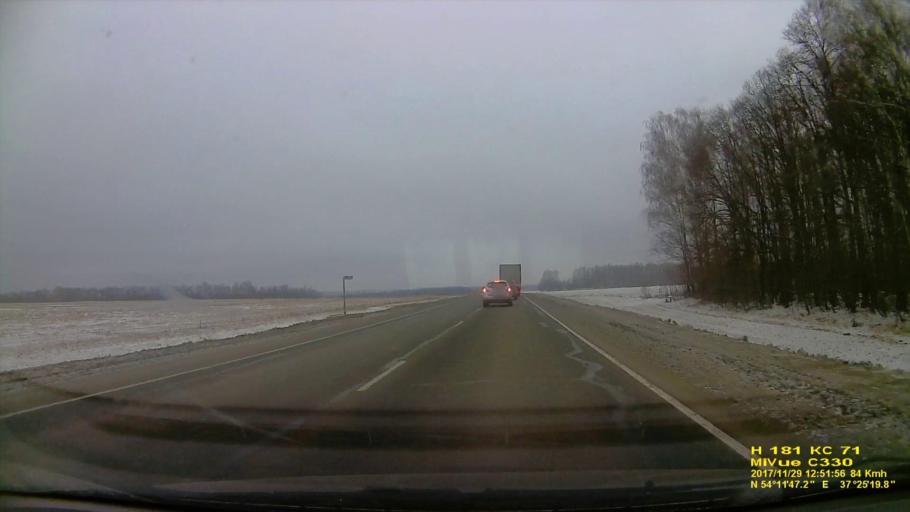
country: RU
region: Tula
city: Barsuki
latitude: 54.1964
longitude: 37.4223
